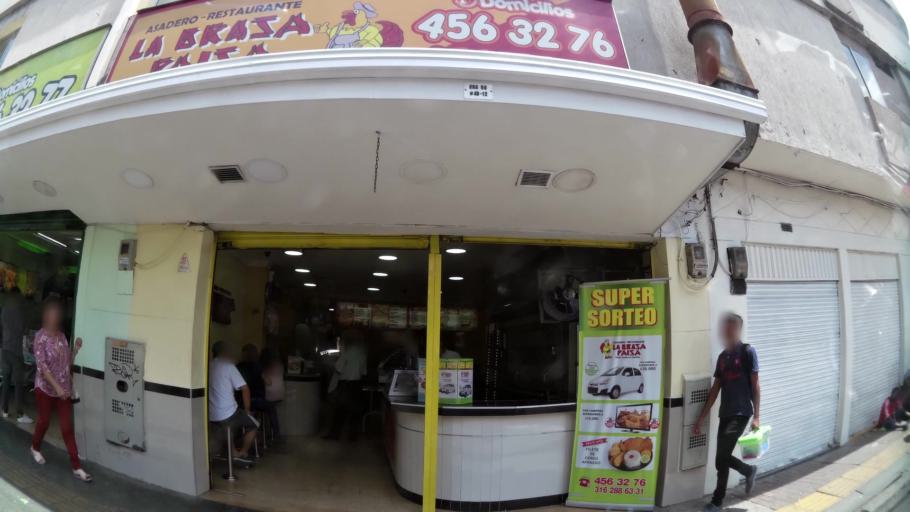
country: CO
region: Antioquia
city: Bello
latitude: 6.3338
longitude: -75.5585
